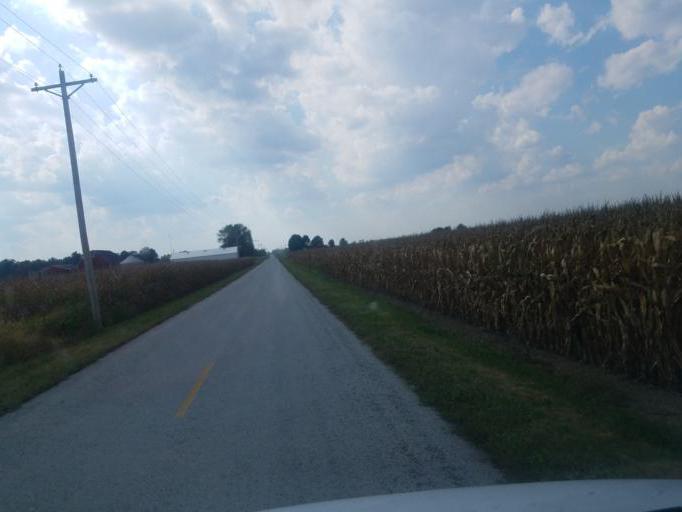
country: US
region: Ohio
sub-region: Hardin County
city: Kenton
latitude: 40.7179
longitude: -83.6080
